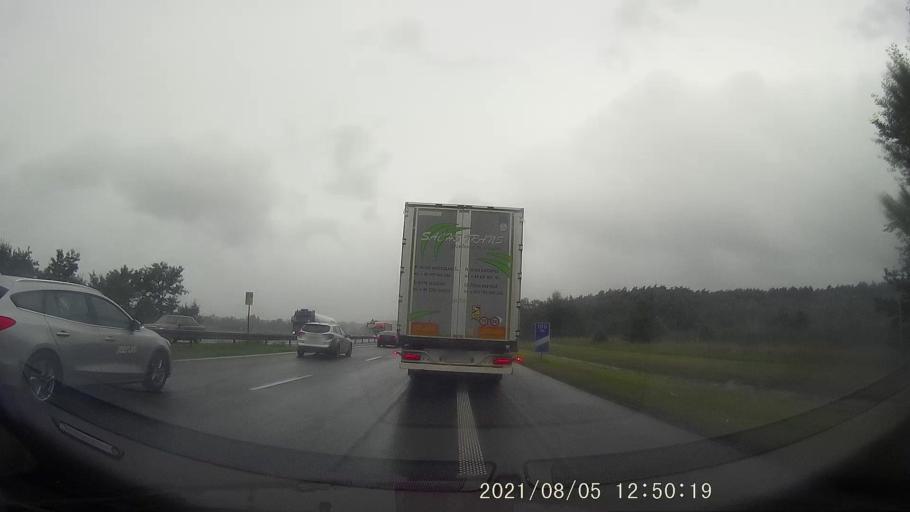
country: PL
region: Opole Voivodeship
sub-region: Powiat krapkowicki
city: Gogolin
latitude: 50.4855
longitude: 18.0019
